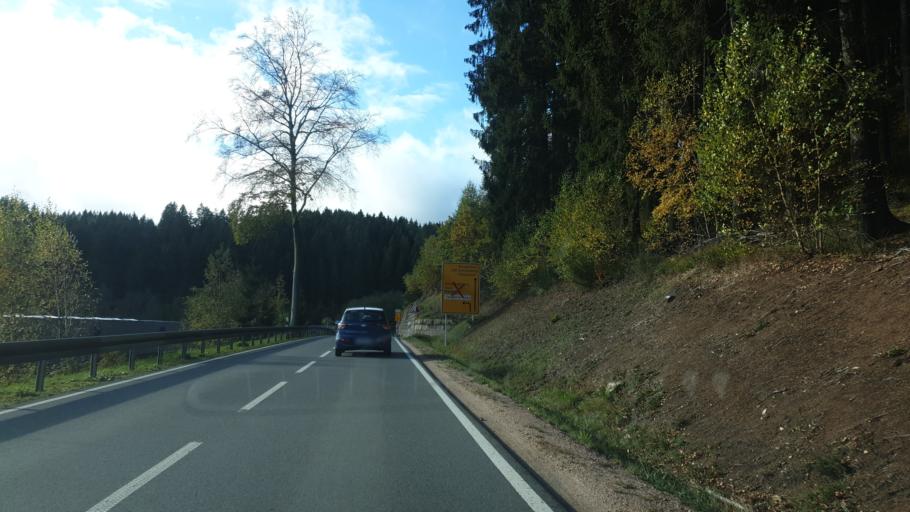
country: DE
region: Saxony
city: Sosa
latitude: 50.5163
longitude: 12.6262
